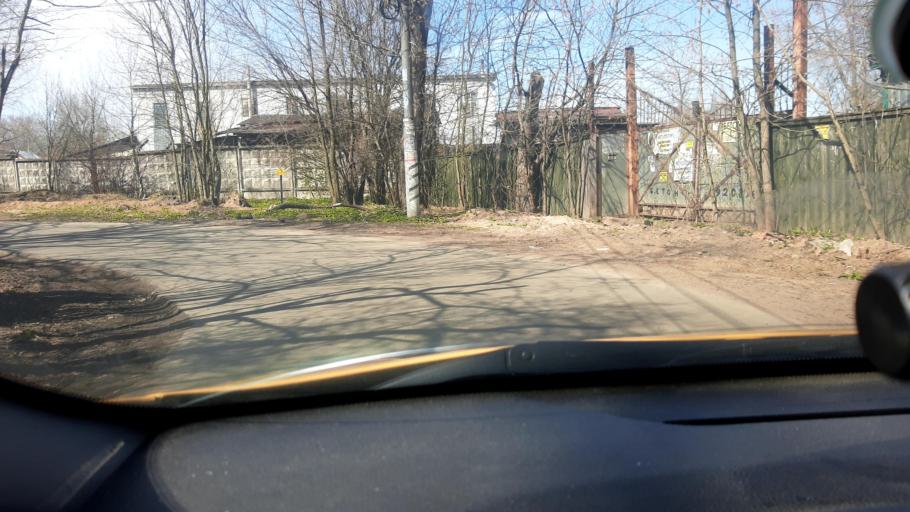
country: RU
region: Moscow
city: Annino
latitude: 55.5327
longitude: 37.6011
